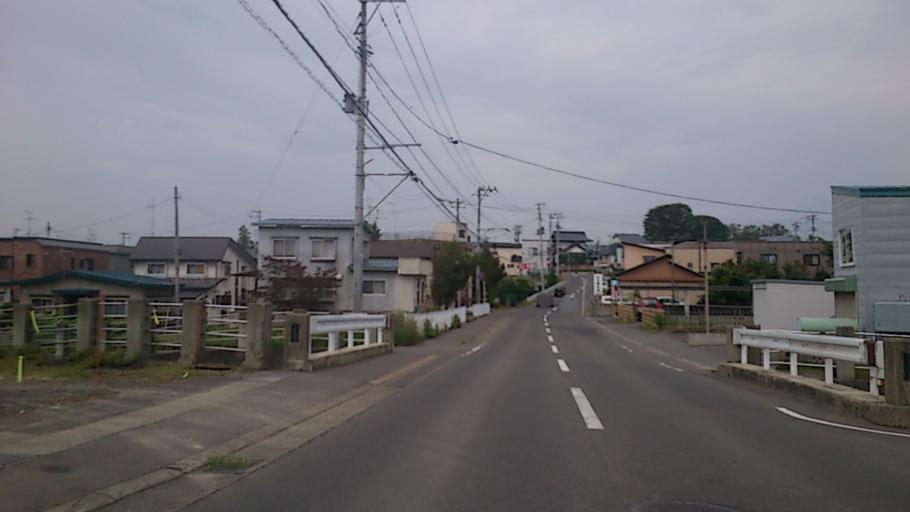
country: JP
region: Aomori
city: Hirosaki
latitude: 40.5943
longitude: 140.4549
